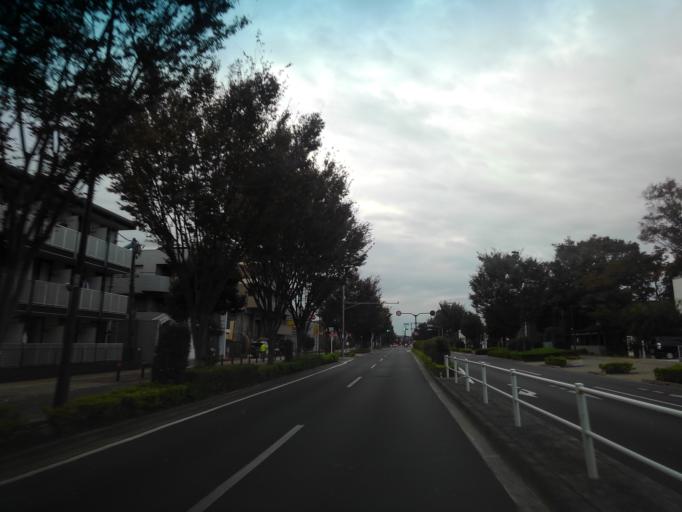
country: JP
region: Tokyo
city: Mitaka-shi
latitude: 35.6764
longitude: 139.5464
